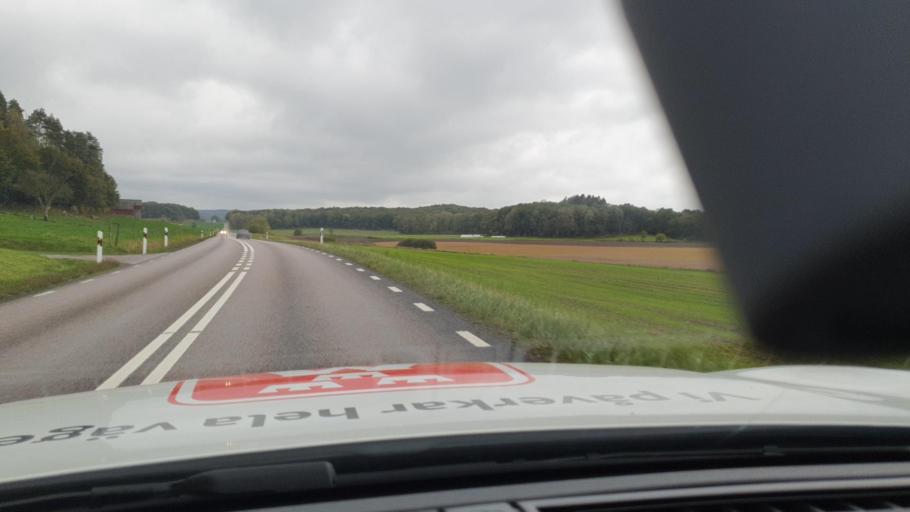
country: SE
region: Halland
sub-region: Falkenbergs Kommun
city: Falkenberg
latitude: 57.0452
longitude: 12.6060
